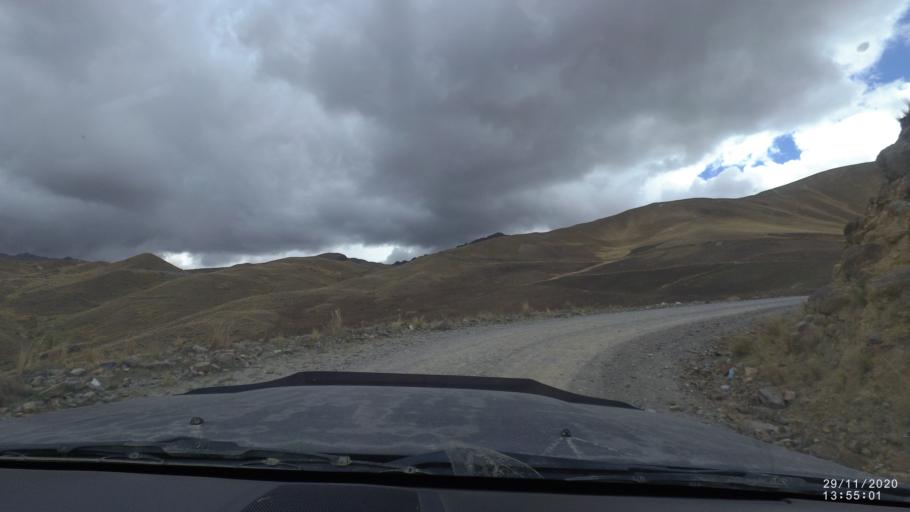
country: BO
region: Cochabamba
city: Sipe Sipe
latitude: -17.1760
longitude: -66.3555
